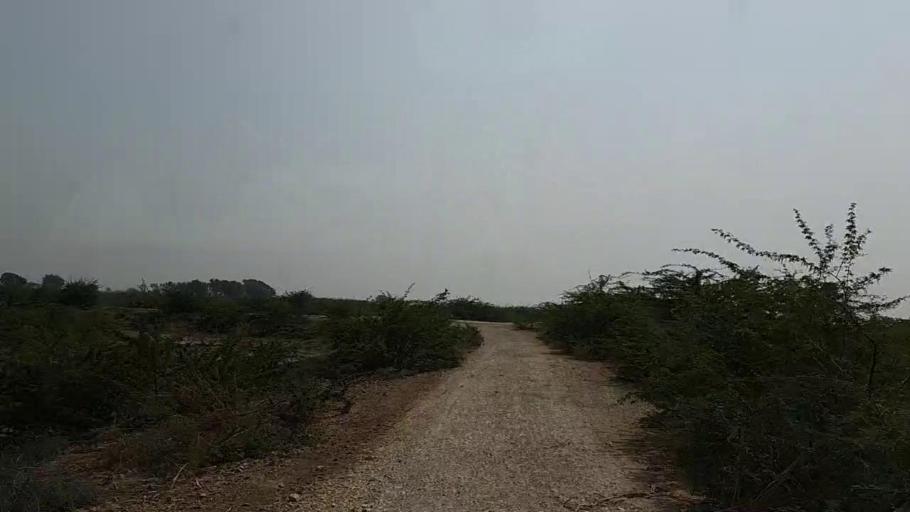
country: PK
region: Sindh
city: Naukot
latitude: 24.7845
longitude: 69.3295
